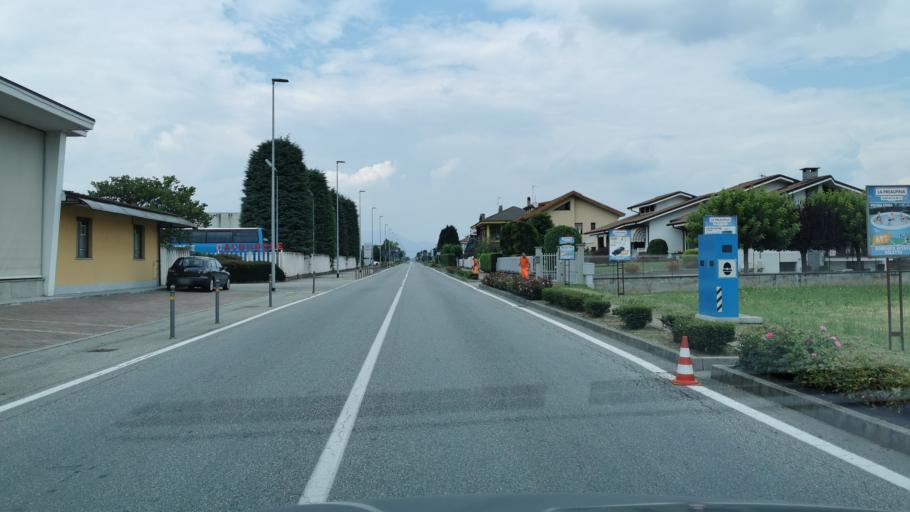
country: IT
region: Piedmont
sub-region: Provincia di Torino
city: Cavour
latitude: 44.7930
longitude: 7.3749
